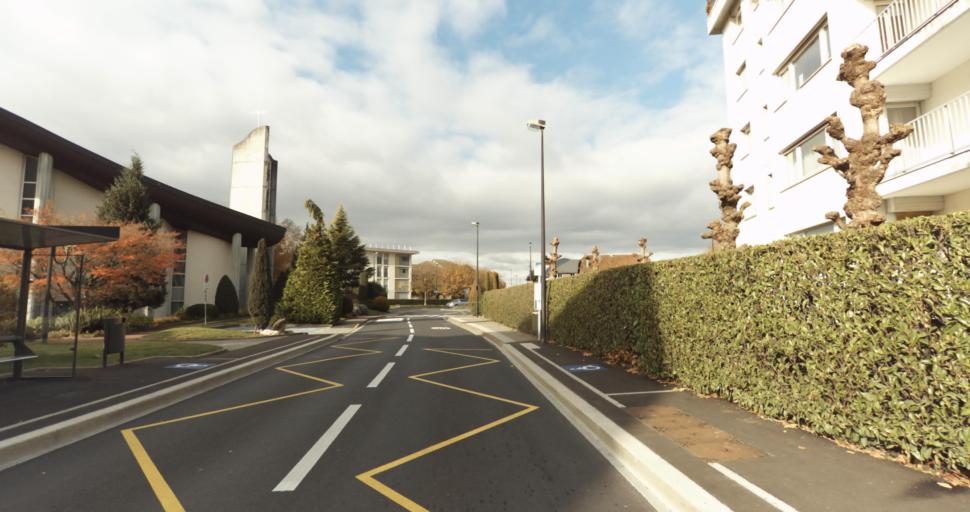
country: FR
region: Rhone-Alpes
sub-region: Departement de la Haute-Savoie
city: Meythet
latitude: 45.9170
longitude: 6.0956
